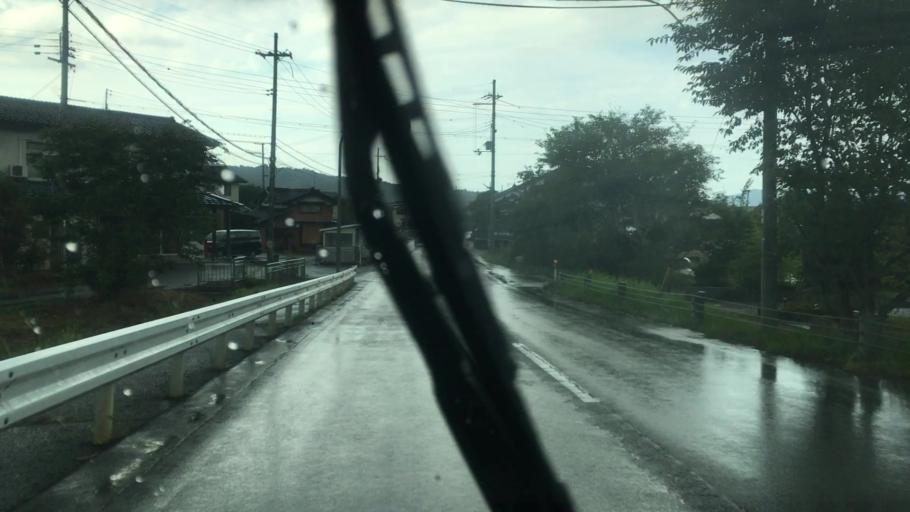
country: JP
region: Hyogo
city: Toyooka
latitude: 35.4897
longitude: 134.8161
